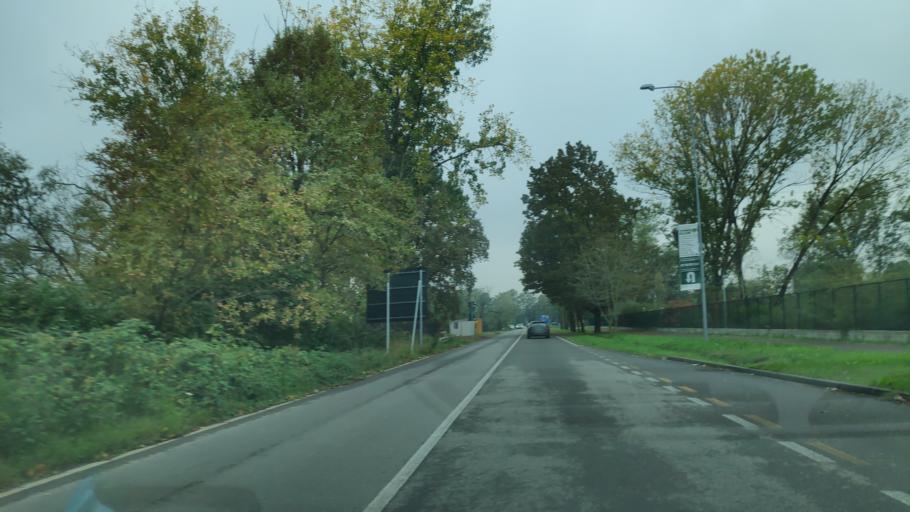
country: IT
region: Lombardy
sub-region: Citta metropolitana di Milano
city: Basiglio
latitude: 45.3686
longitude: 9.1714
